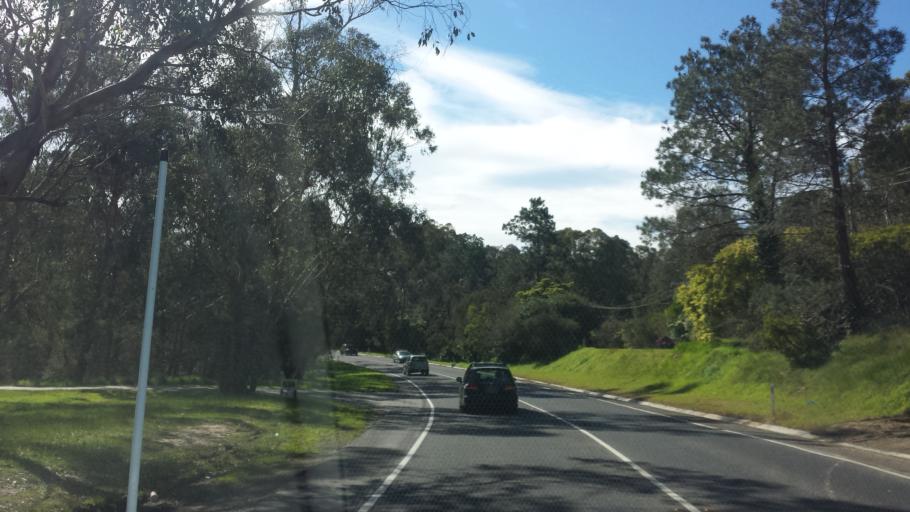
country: AU
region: Victoria
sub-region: Maroondah
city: Warranwood
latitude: -37.7826
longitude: 145.2339
